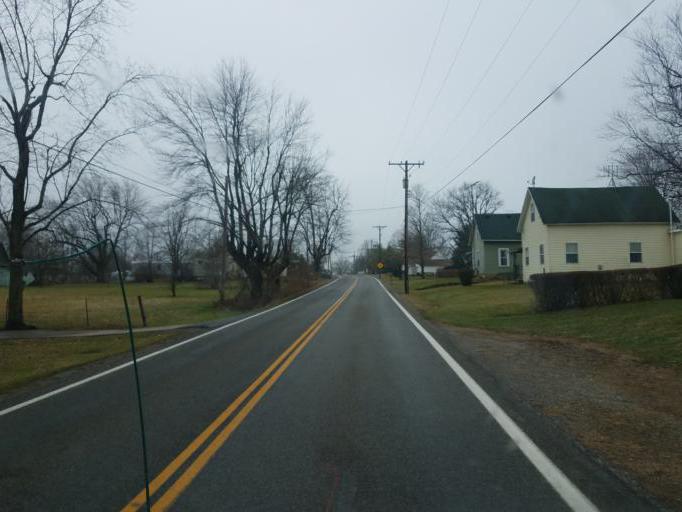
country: US
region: Ohio
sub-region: Champaign County
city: North Lewisburg
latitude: 40.2936
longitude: -83.5796
